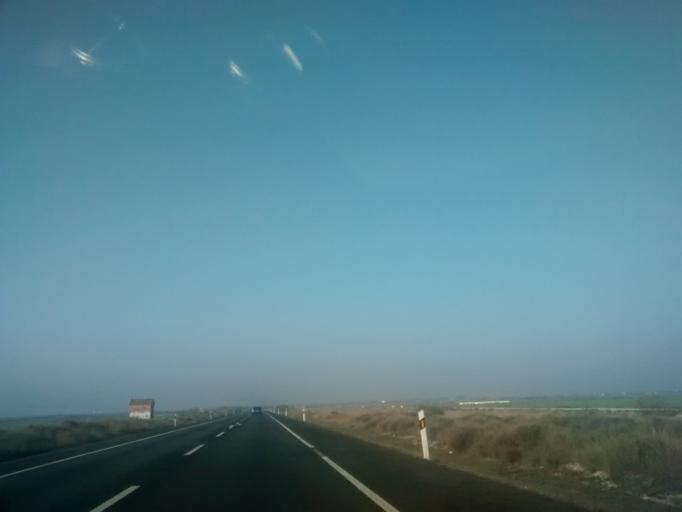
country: ES
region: Aragon
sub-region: Provincia de Huesca
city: Candasnos
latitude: 41.5185
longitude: 0.1373
